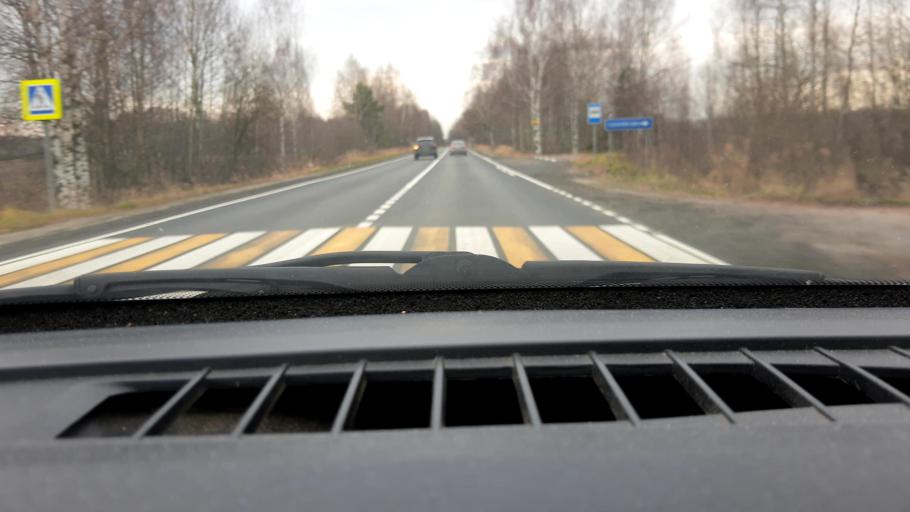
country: RU
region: Nizjnij Novgorod
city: Novaya Balakhna
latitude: 56.5500
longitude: 43.7513
